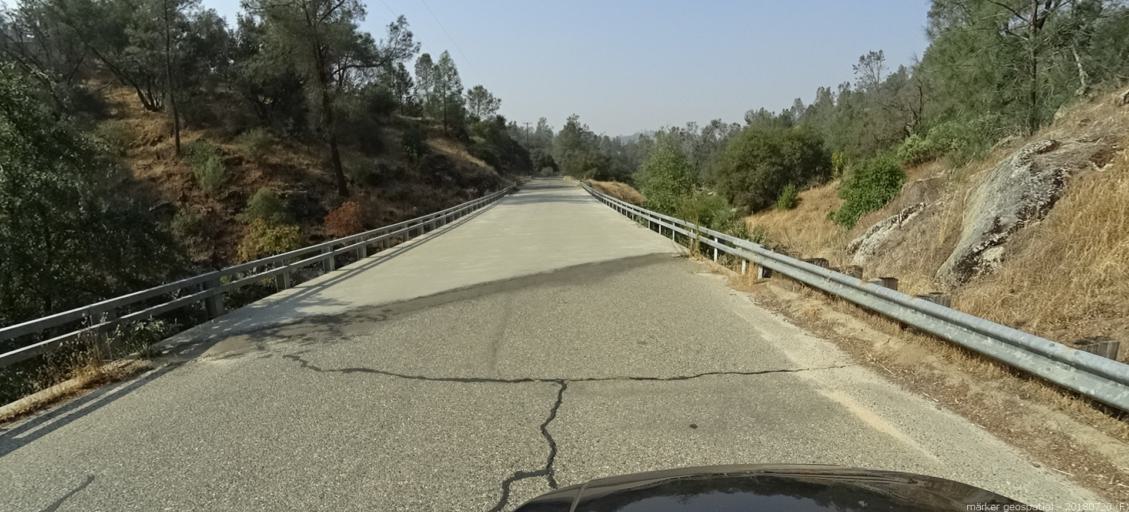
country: US
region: California
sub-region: Madera County
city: Yosemite Lakes
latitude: 37.2888
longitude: -119.8687
